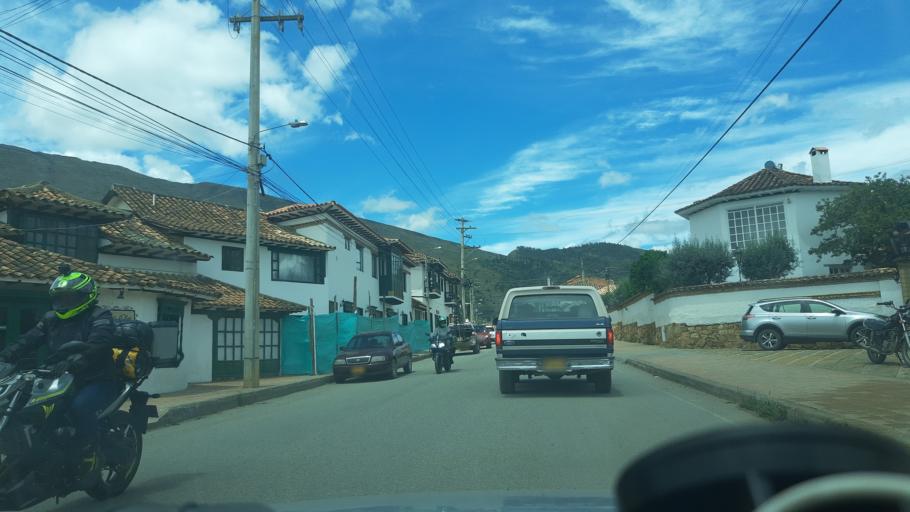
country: CO
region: Boyaca
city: Villa de Leiva
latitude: 5.6332
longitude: -73.5279
